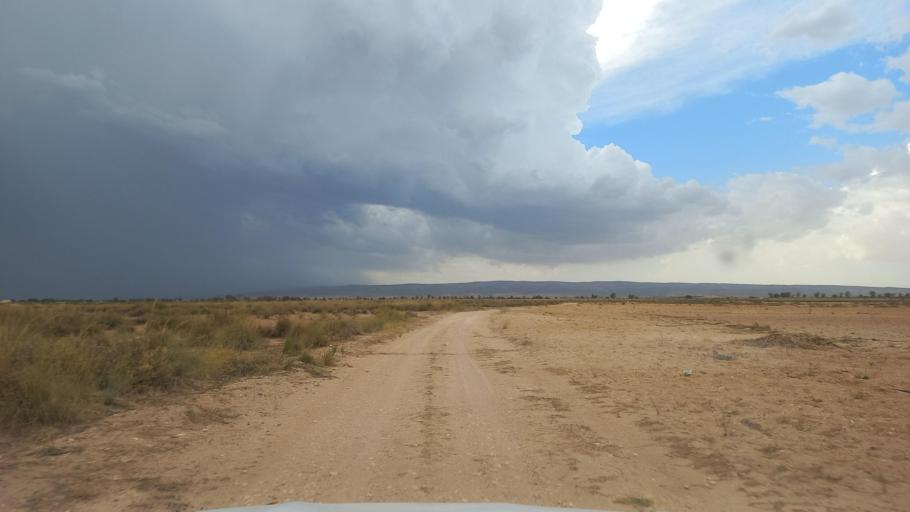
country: TN
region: Al Qasrayn
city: Kasserine
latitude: 35.2389
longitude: 9.0123
